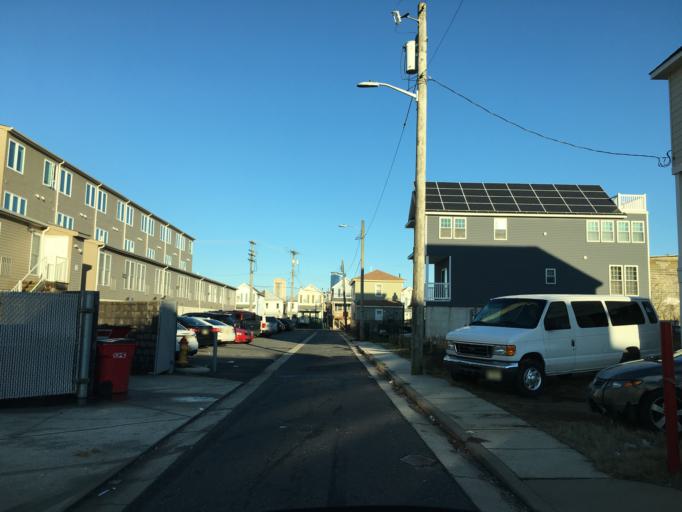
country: US
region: New Jersey
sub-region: Atlantic County
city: Atlantic City
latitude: 39.3699
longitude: -74.4197
